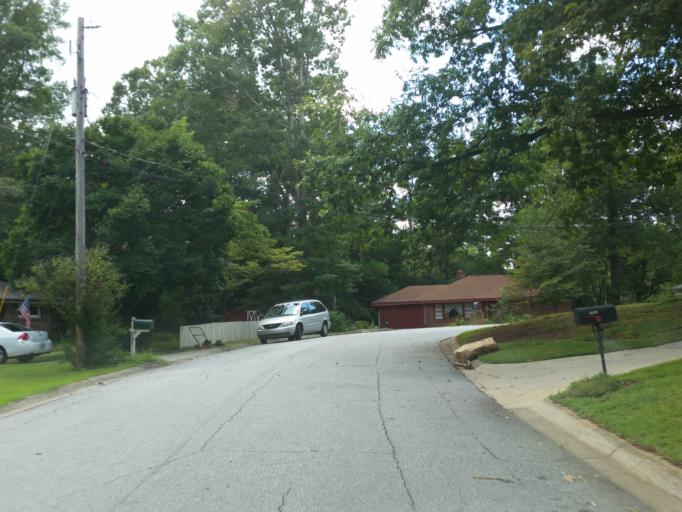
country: US
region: Georgia
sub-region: Cobb County
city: Smyrna
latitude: 33.8735
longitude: -84.5213
